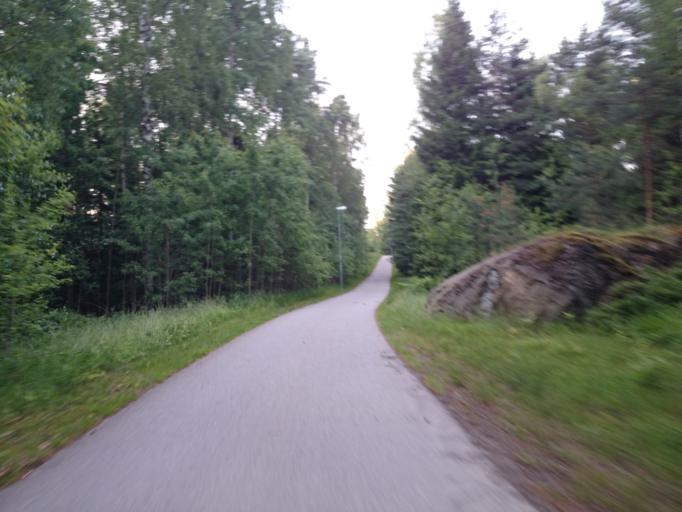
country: SE
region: Stockholm
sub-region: Botkyrka Kommun
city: Fittja
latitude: 59.2583
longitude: 17.8893
